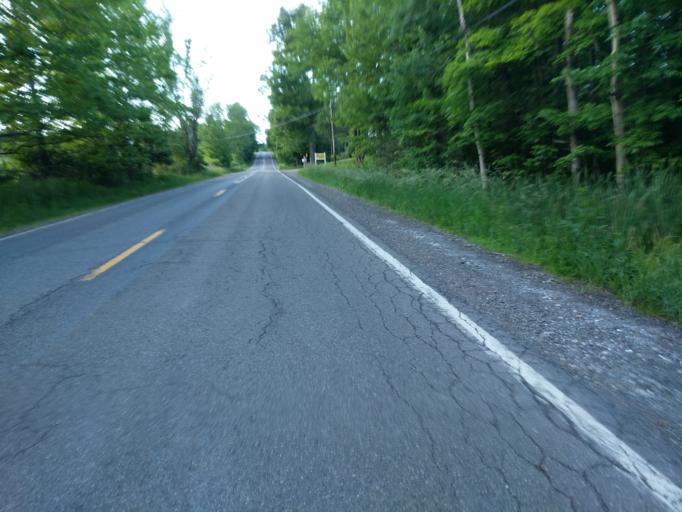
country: US
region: New York
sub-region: Tompkins County
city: Dryden
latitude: 42.4059
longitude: -76.3505
